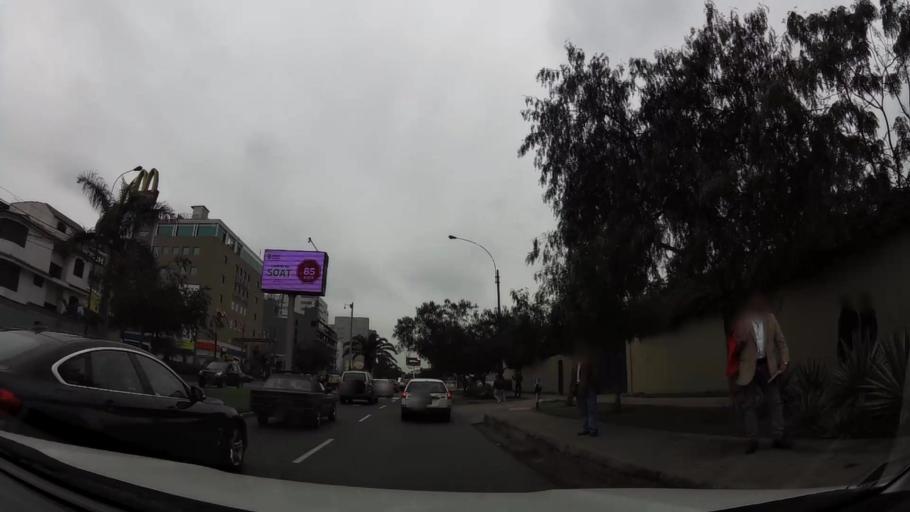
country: PE
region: Lima
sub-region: Lima
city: La Molina
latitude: -12.1023
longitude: -76.9704
